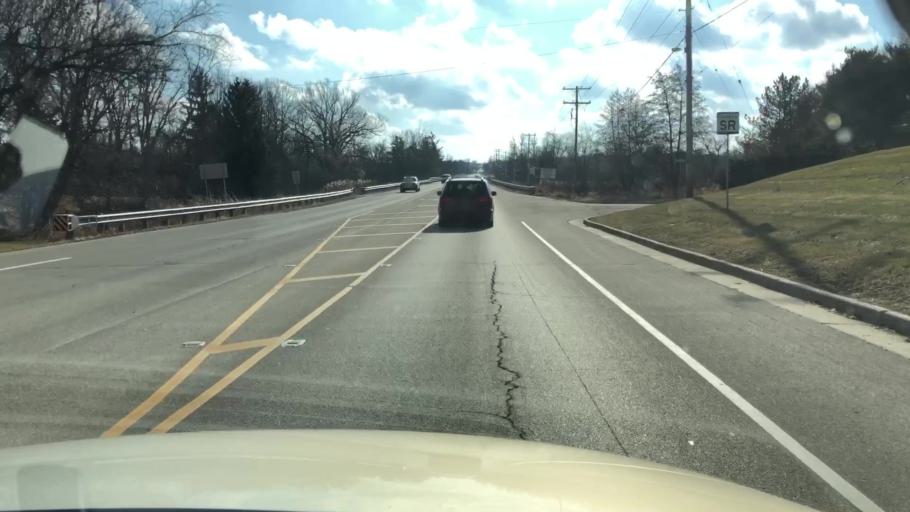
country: US
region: Wisconsin
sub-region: Waukesha County
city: Waukesha
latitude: 43.0571
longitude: -88.1859
